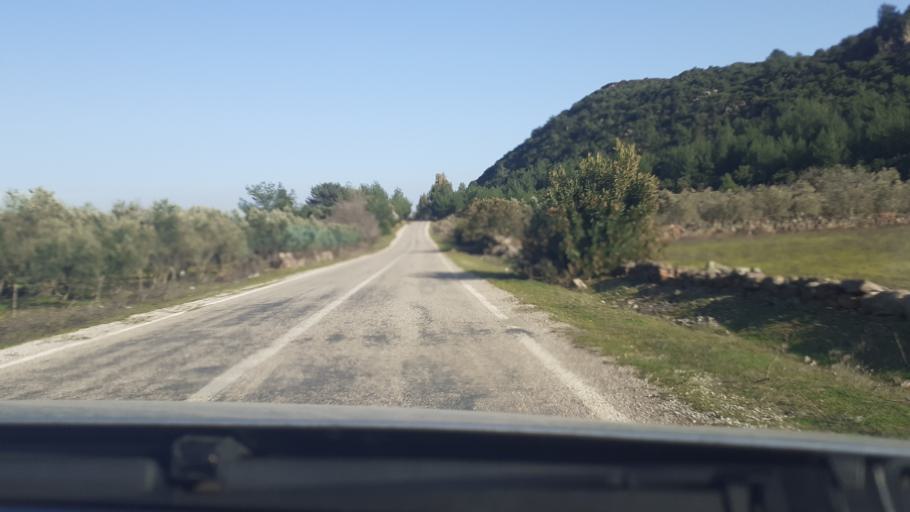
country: TR
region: Hatay
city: Aktepe
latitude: 36.7334
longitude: 36.4705
